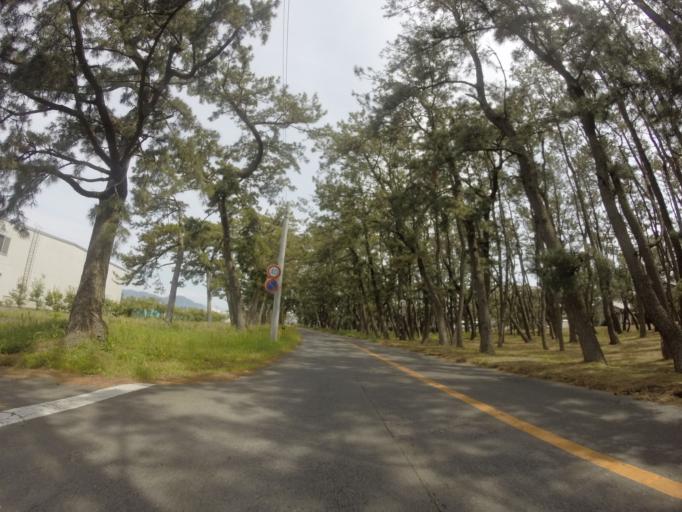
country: JP
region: Shizuoka
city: Yaizu
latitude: 34.8253
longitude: 138.3327
